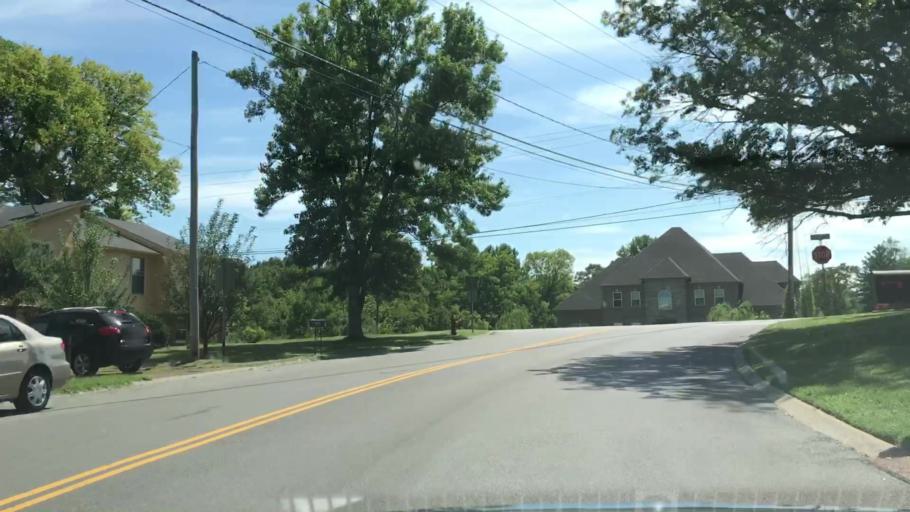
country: US
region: Tennessee
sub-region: Williamson County
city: Brentwood Estates
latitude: 36.0328
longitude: -86.7079
